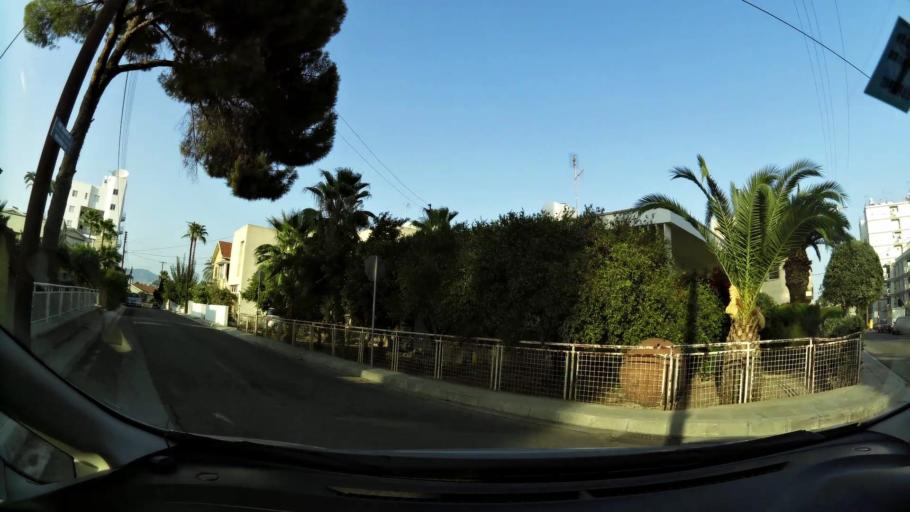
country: CY
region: Lefkosia
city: Nicosia
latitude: 35.1700
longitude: 33.3379
